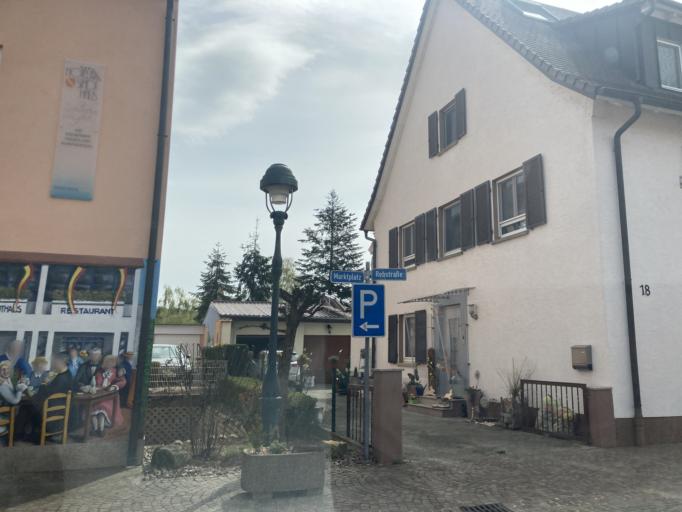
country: DE
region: Baden-Wuerttemberg
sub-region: Freiburg Region
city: Neuenburg am Rhein
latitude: 47.8154
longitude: 7.5629
